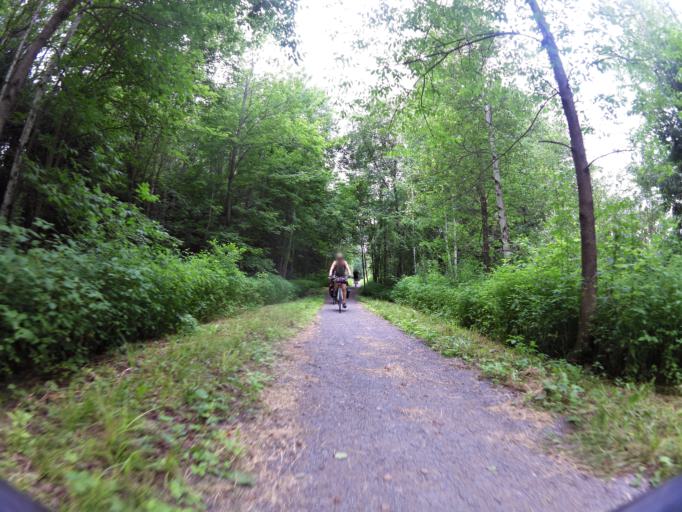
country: CA
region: Ontario
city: Bells Corners
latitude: 45.0254
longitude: -75.6817
